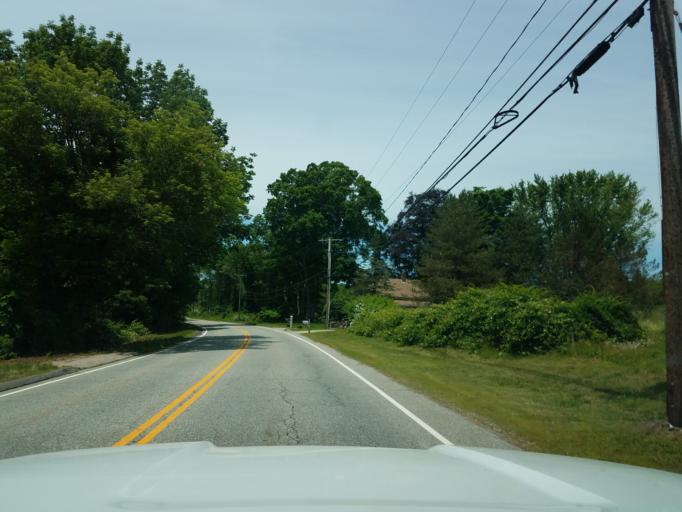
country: US
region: Connecticut
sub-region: Windham County
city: Willimantic
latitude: 41.6665
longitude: -72.2555
